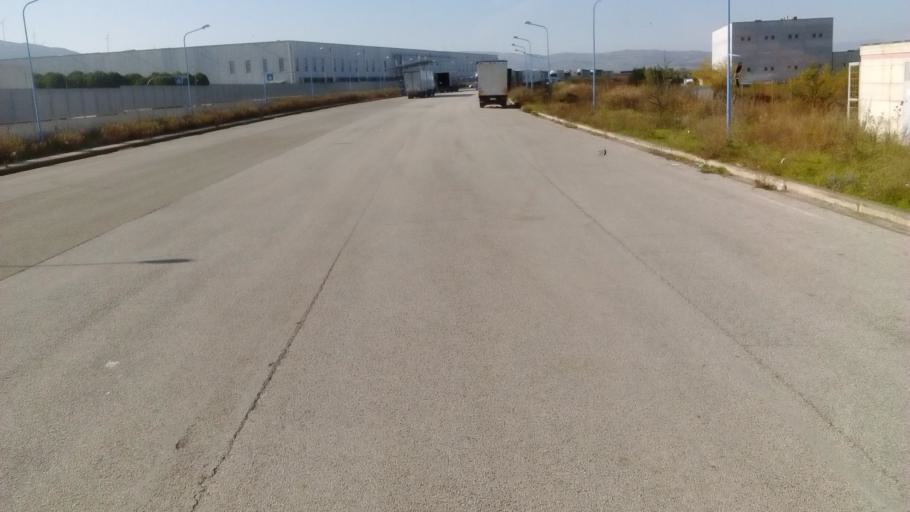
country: IT
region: Basilicate
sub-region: Provincia di Potenza
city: Melfi
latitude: 41.0782
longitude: 15.6562
